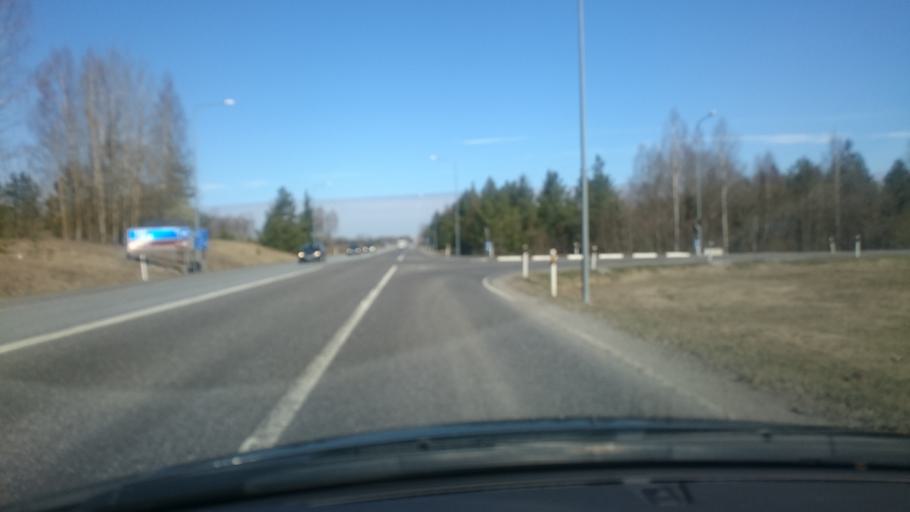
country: EE
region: Raplamaa
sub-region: Rapla vald
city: Rapla
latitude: 59.0876
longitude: 24.8020
